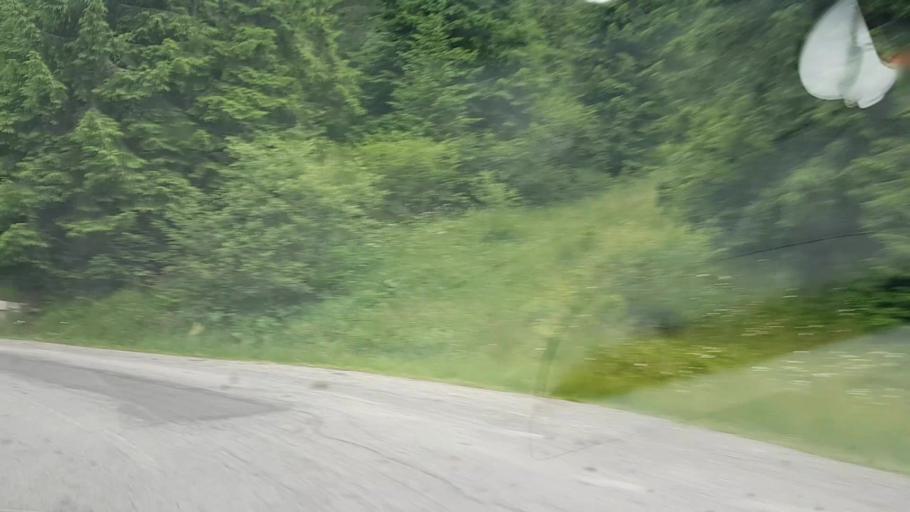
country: RO
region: Harghita
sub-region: Municipiul Gheorgheni
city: Gheorgheni
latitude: 46.7798
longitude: 25.7199
